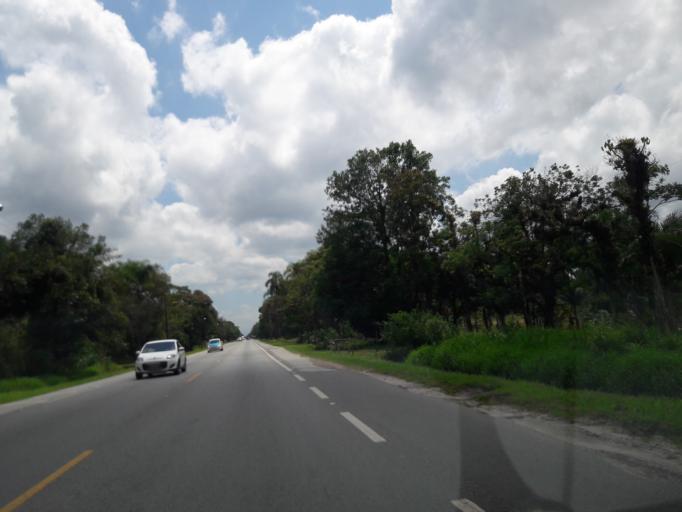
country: BR
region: Parana
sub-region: Pontal Do Parana
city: Pontal do Parana
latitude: -25.6384
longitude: -48.5347
